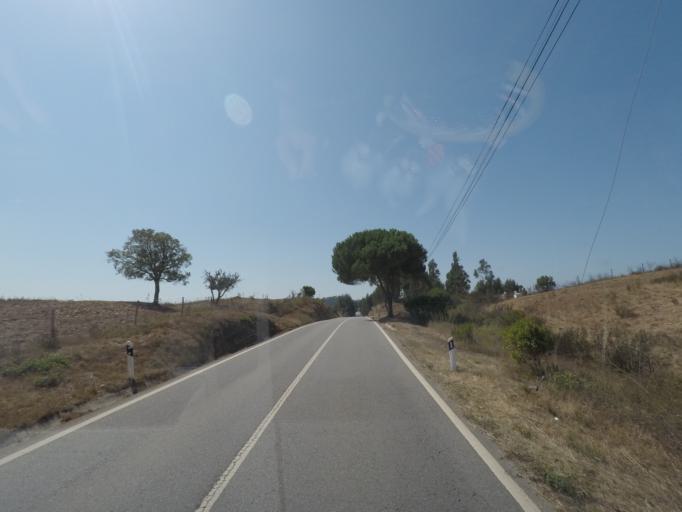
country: PT
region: Beja
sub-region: Odemira
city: Sao Teotonio
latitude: 37.5415
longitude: -8.6888
